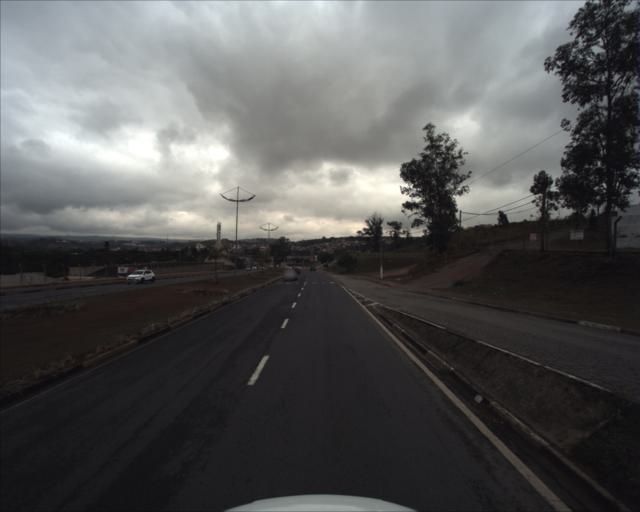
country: BR
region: Sao Paulo
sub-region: Votorantim
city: Votorantim
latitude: -23.5306
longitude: -47.4503
